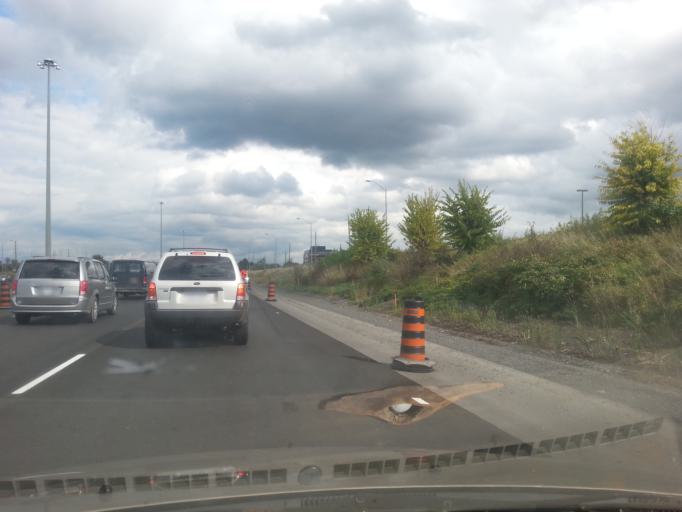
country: CA
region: Ontario
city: Bells Corners
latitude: 45.3118
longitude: -75.9007
